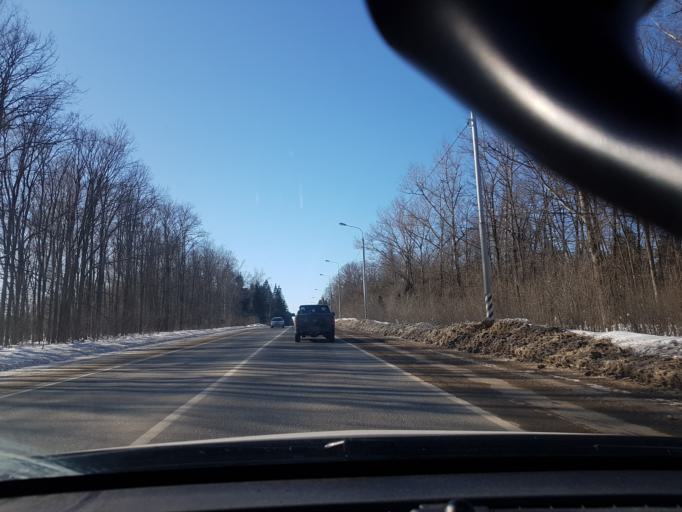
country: RU
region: Moskovskaya
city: Kostrovo
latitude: 55.9126
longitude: 36.7506
